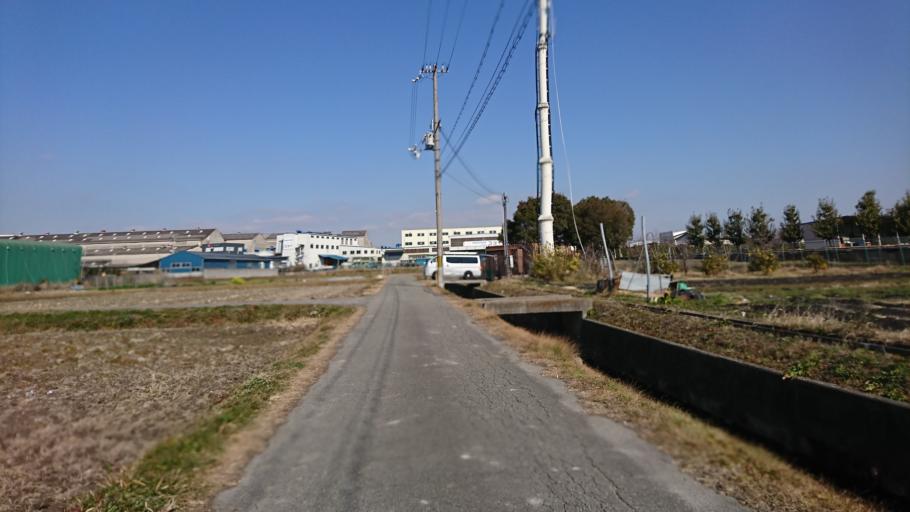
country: JP
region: Hyogo
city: Kakogawacho-honmachi
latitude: 34.7292
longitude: 134.8652
